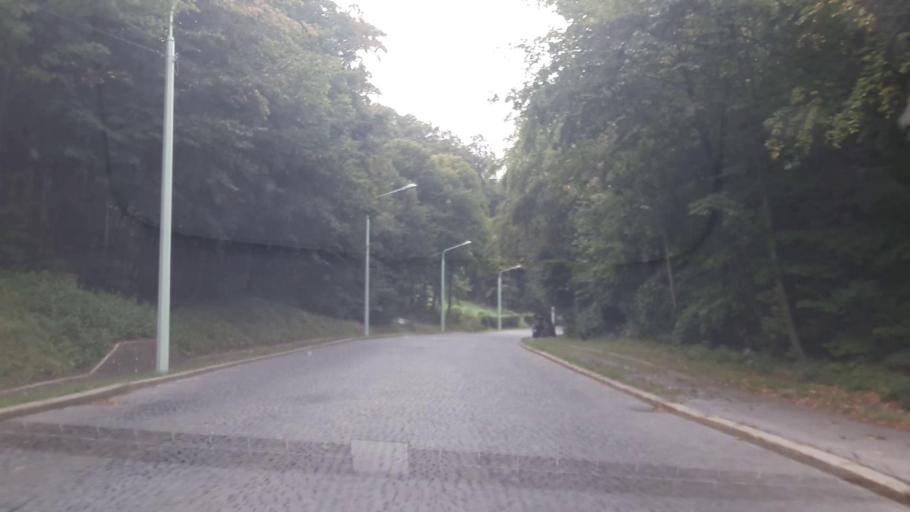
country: AT
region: Lower Austria
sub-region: Politischer Bezirk Wien-Umgebung
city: Klosterneuburg
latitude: 48.2668
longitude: 16.3227
